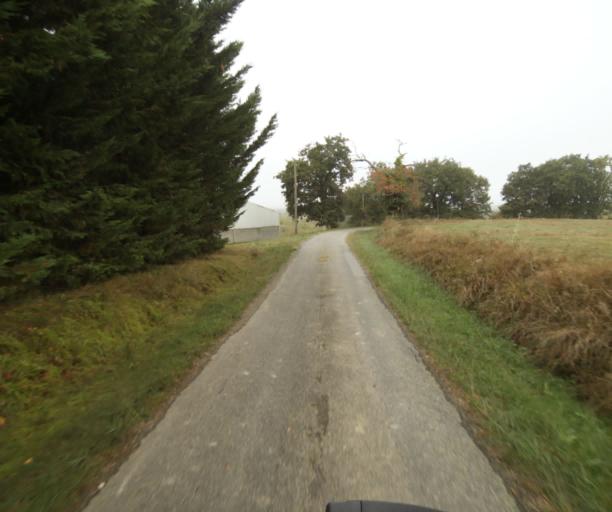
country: FR
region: Midi-Pyrenees
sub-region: Departement du Tarn-et-Garonne
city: Nohic
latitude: 43.9276
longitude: 1.4681
